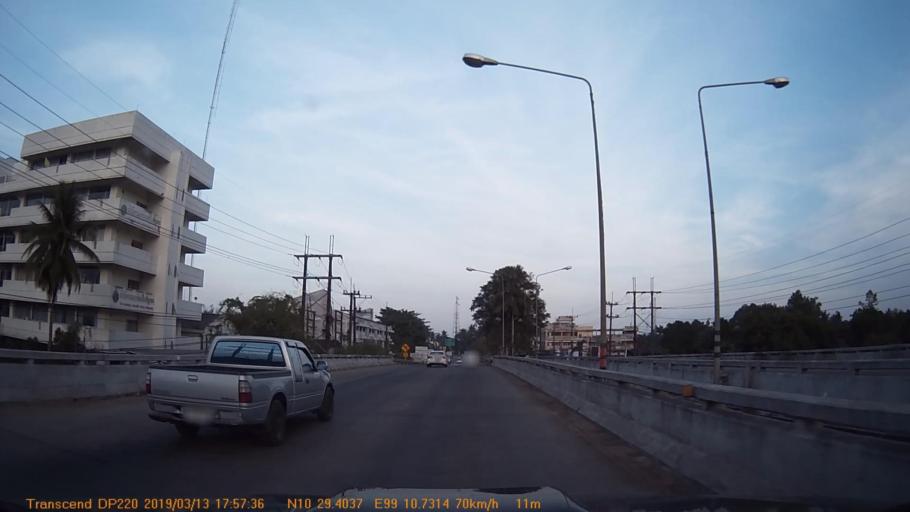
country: TH
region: Chumphon
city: Chumphon
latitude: 10.4900
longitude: 99.1792
